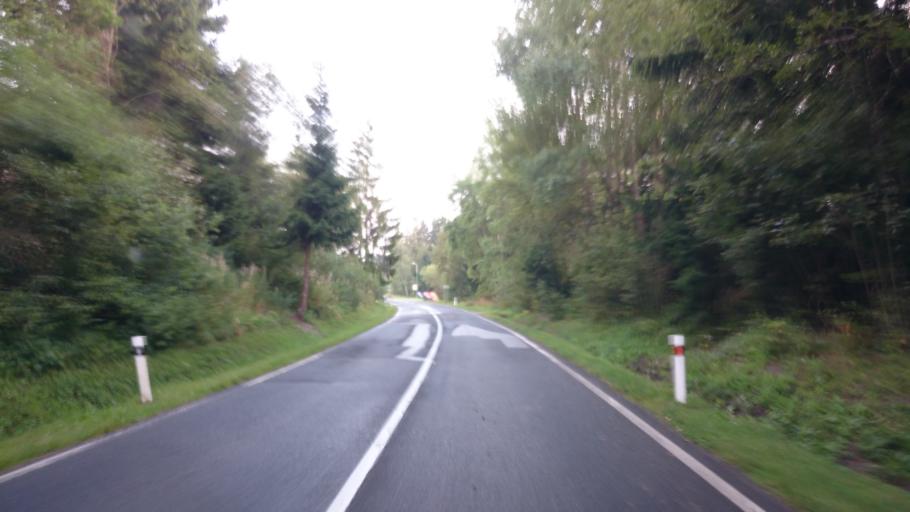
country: SK
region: Presovsky
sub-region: Okres Poprad
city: Strba
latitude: 49.0949
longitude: 20.0684
